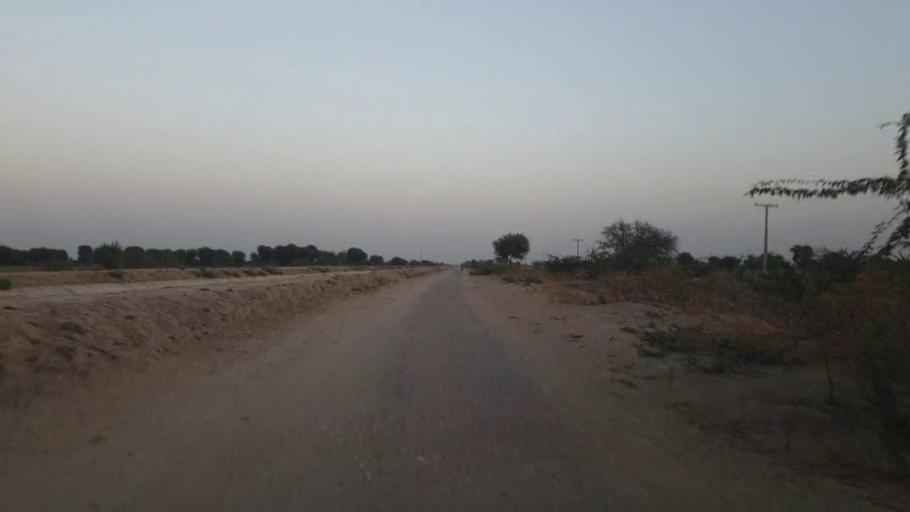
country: PK
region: Sindh
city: Umarkot
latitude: 25.4183
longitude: 69.6700
